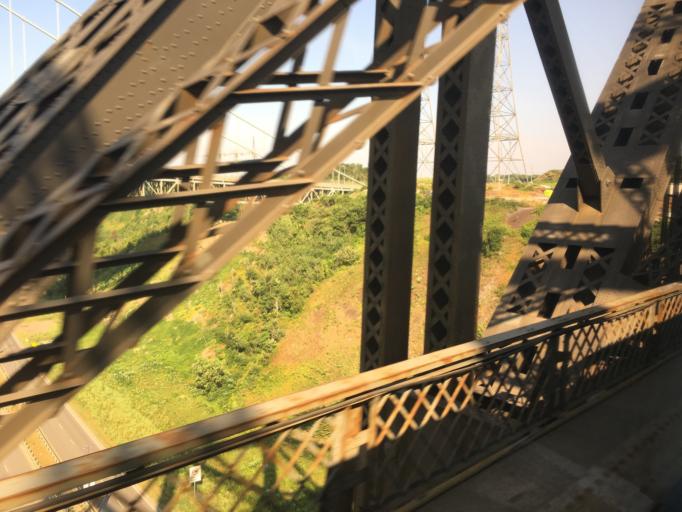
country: CA
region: Quebec
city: L'Ancienne-Lorette
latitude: 46.7486
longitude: -71.2899
